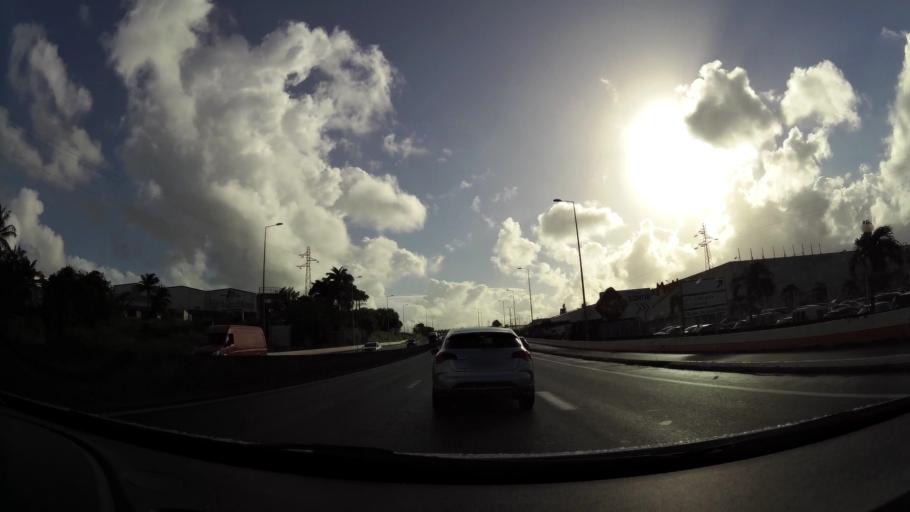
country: MQ
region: Martinique
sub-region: Martinique
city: Le Lamentin
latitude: 14.6181
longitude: -61.0343
